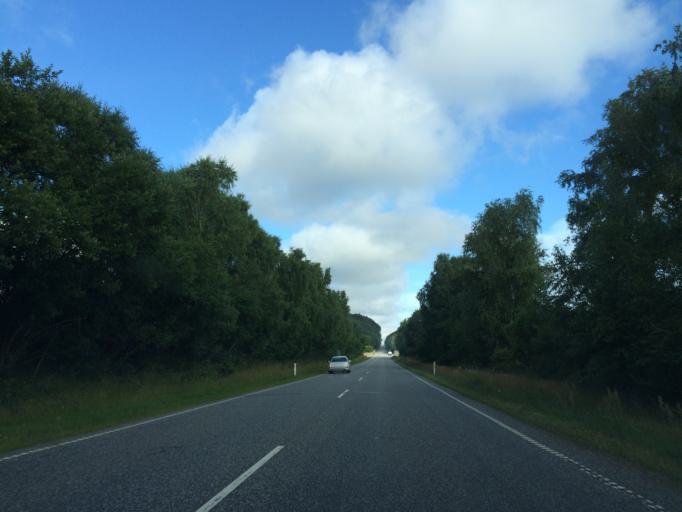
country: DK
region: Central Jutland
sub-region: Viborg Kommune
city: Bjerringbro
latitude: 56.3162
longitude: 9.5788
